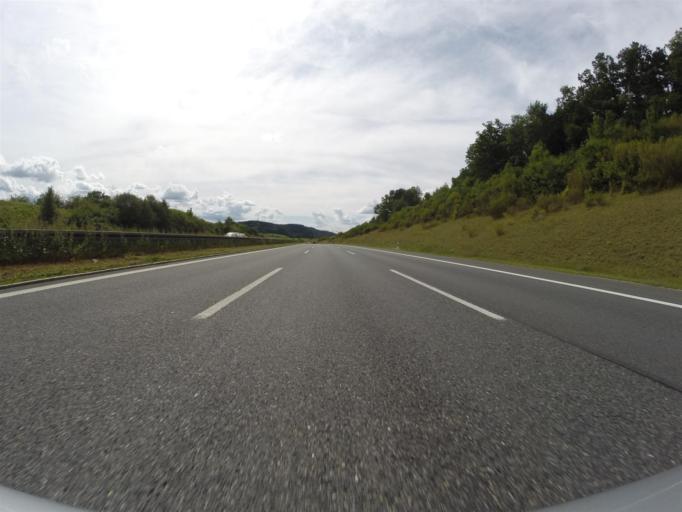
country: DE
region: Bavaria
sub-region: Upper Franconia
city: Haag
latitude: 49.8818
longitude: 11.5577
